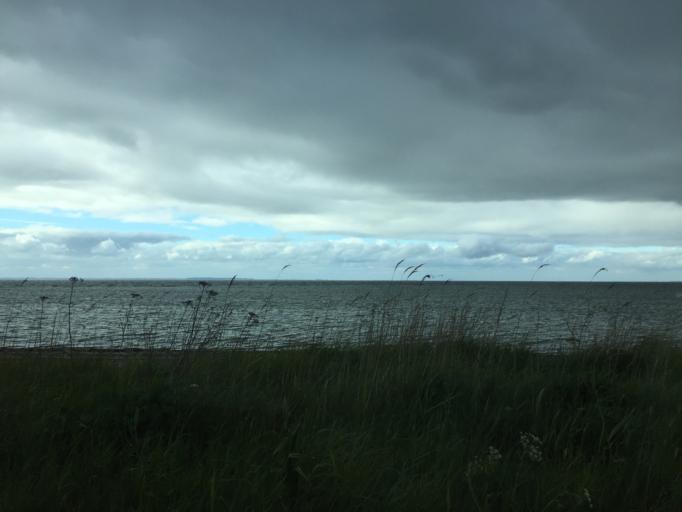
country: DK
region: South Denmark
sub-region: Sonderborg Kommune
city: Nordborg
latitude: 55.0834
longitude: 9.7411
